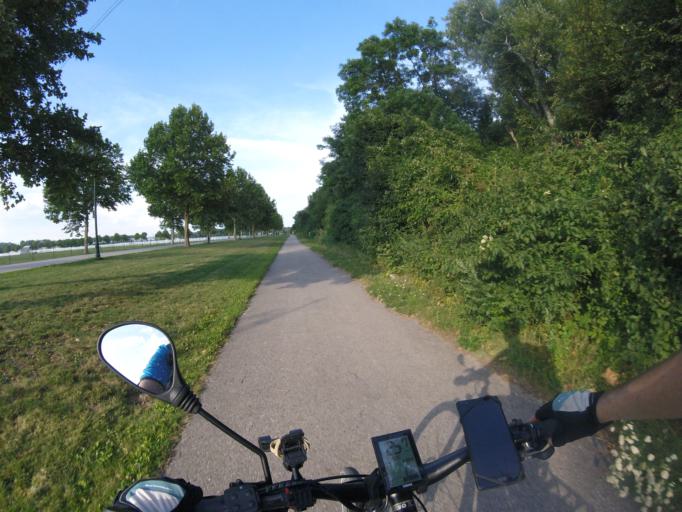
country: AT
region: Lower Austria
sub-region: Politischer Bezirk Baden
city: Ebreichsdorf
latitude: 47.9661
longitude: 16.3756
